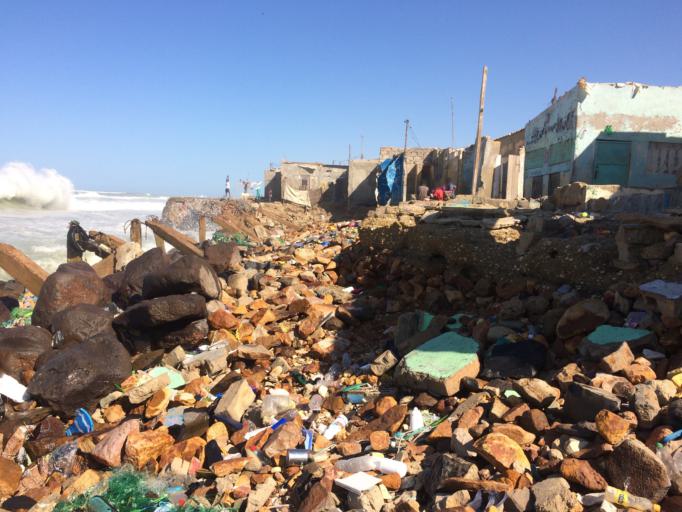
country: SN
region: Saint-Louis
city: Saint-Louis
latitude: 16.0254
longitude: -16.5093
